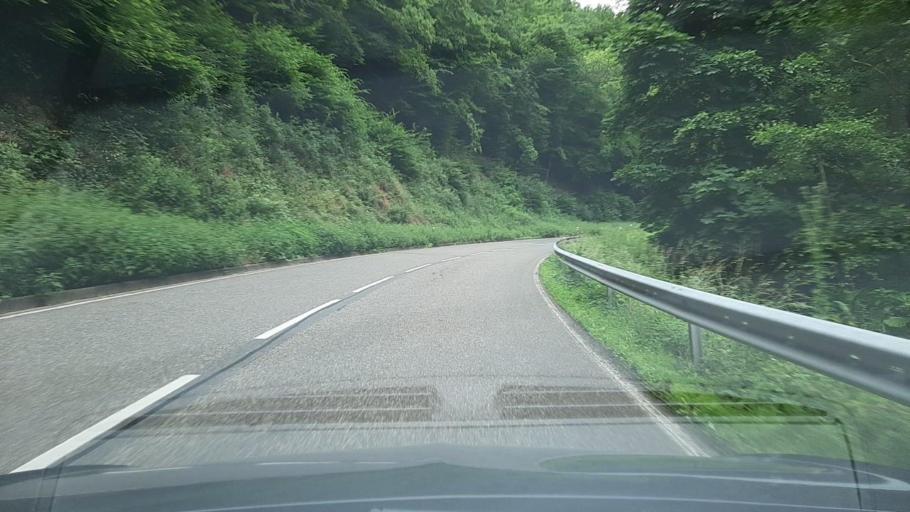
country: DE
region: Rheinland-Pfalz
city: Burgen
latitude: 50.2017
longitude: 7.4051
